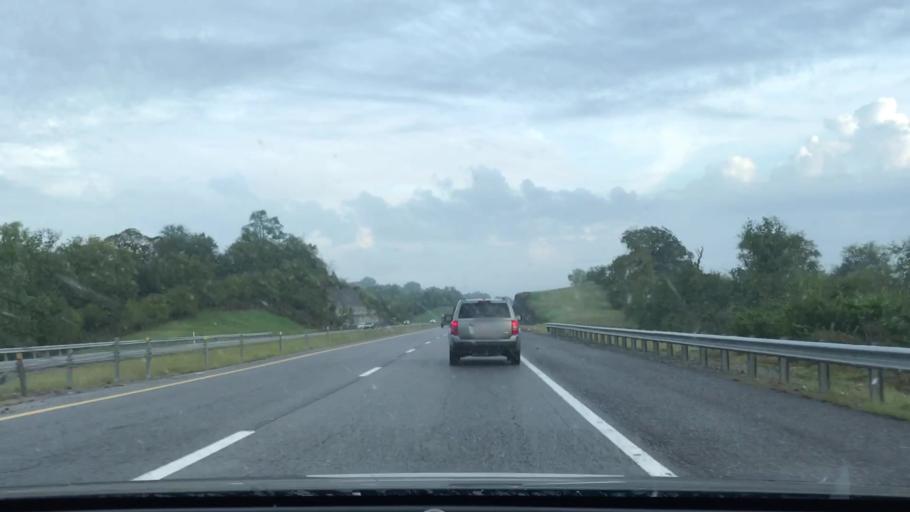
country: US
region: Tennessee
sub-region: Sumner County
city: Shackle Island
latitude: 36.3376
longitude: -86.5492
